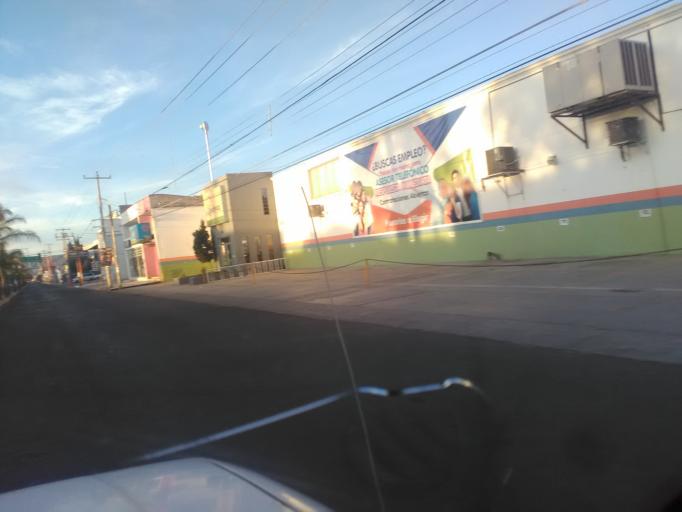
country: MX
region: Durango
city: Victoria de Durango
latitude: 23.9967
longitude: -104.6628
